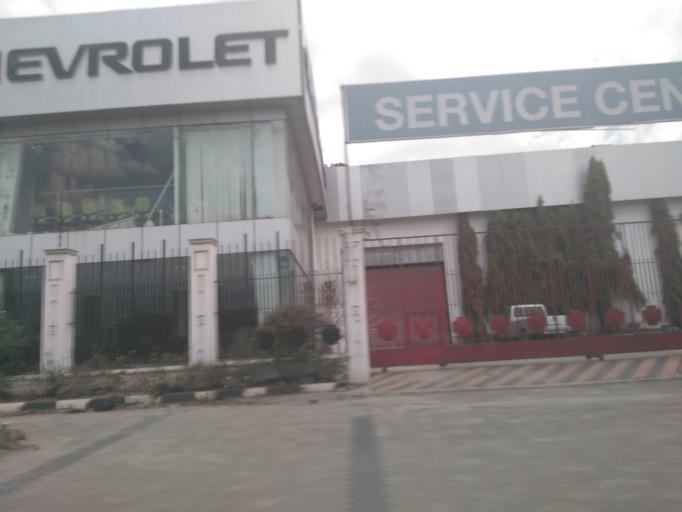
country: TZ
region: Dar es Salaam
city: Dar es Salaam
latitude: -6.8356
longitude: 39.2635
